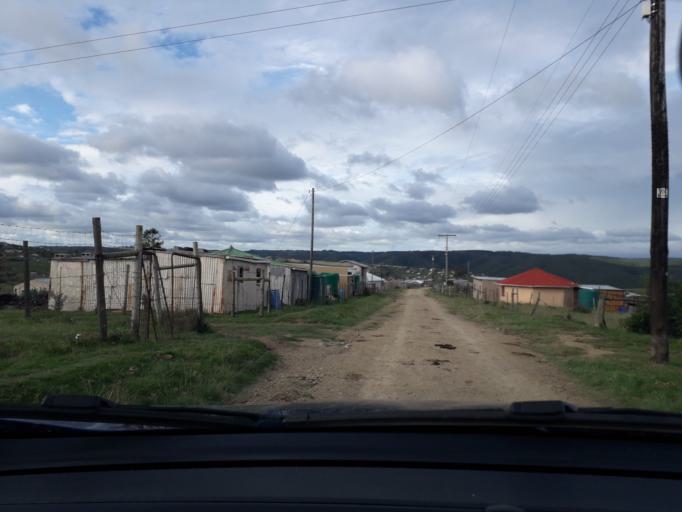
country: ZA
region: Eastern Cape
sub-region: Buffalo City Metropolitan Municipality
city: East London
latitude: -32.8045
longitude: 27.9617
